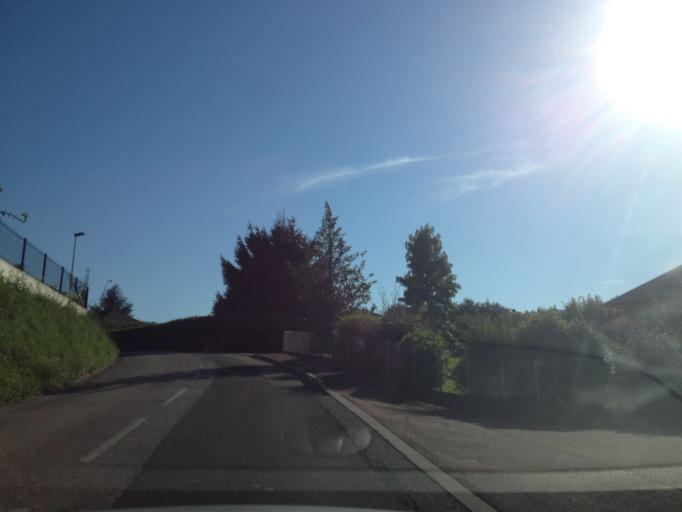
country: FR
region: Rhone-Alpes
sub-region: Departement de la Savoie
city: Voglans
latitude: 45.6290
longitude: 5.8994
